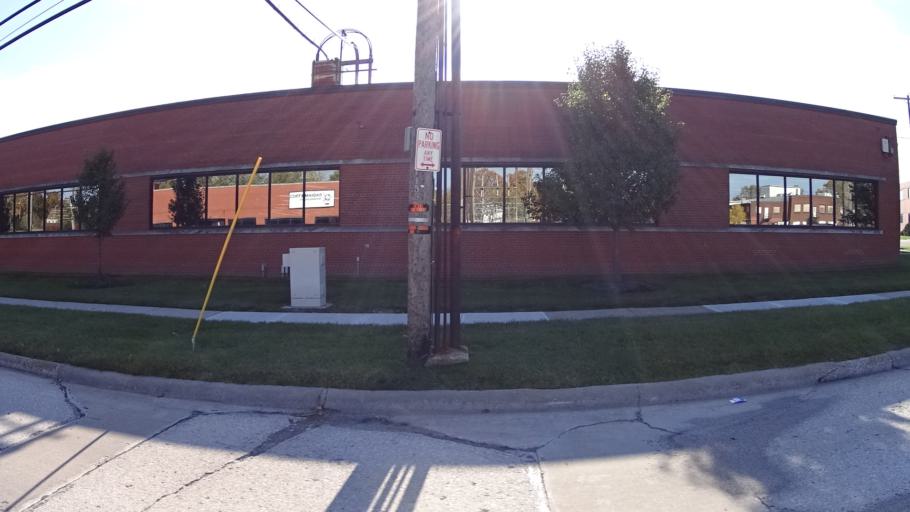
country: US
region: Ohio
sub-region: Lorain County
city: Lorain
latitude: 41.4691
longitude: -82.1587
